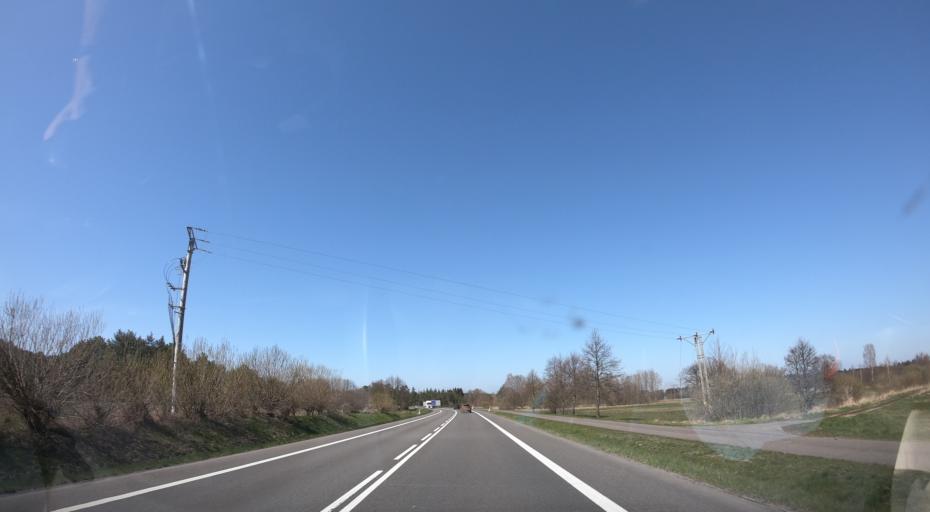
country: PL
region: West Pomeranian Voivodeship
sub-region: Powiat kamienski
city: Wolin
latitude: 53.8767
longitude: 14.5355
